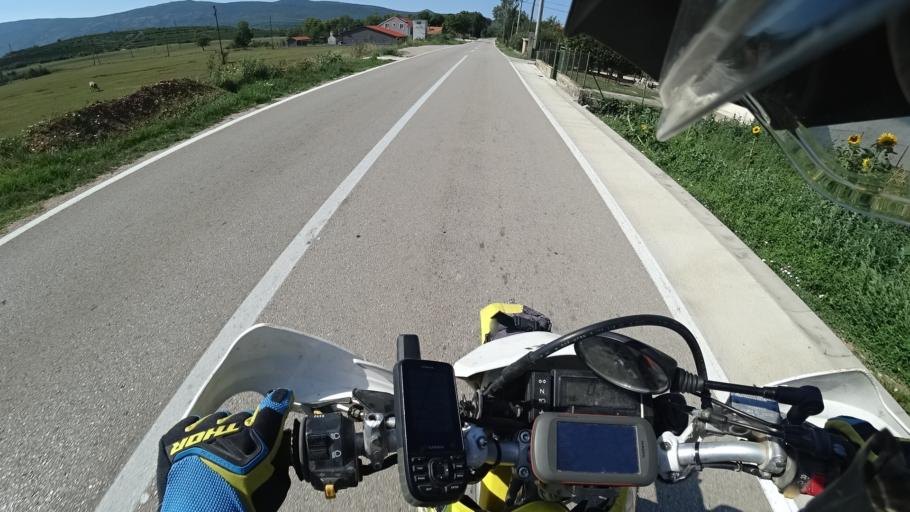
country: HR
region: Sibensko-Kniniska
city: Drnis
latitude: 43.8701
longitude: 16.1942
